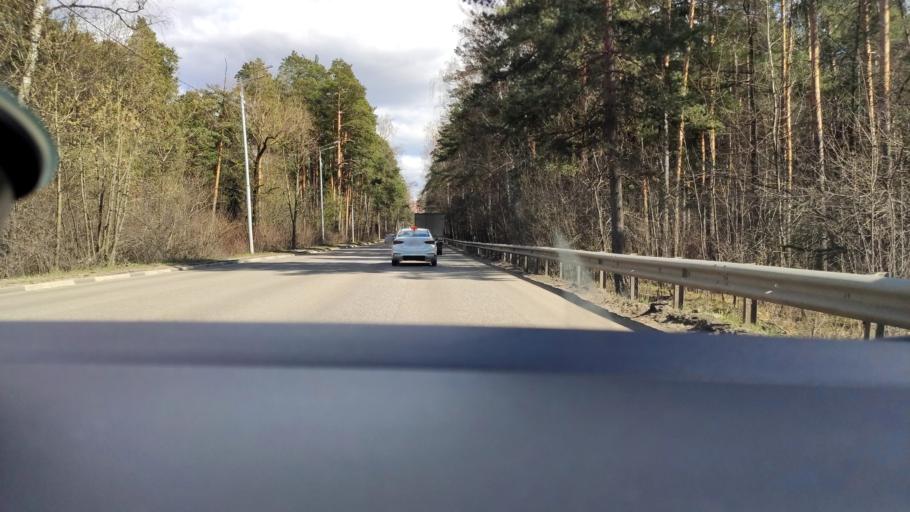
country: RU
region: Moscow
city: Vostochnyy
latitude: 55.8267
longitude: 37.9036
